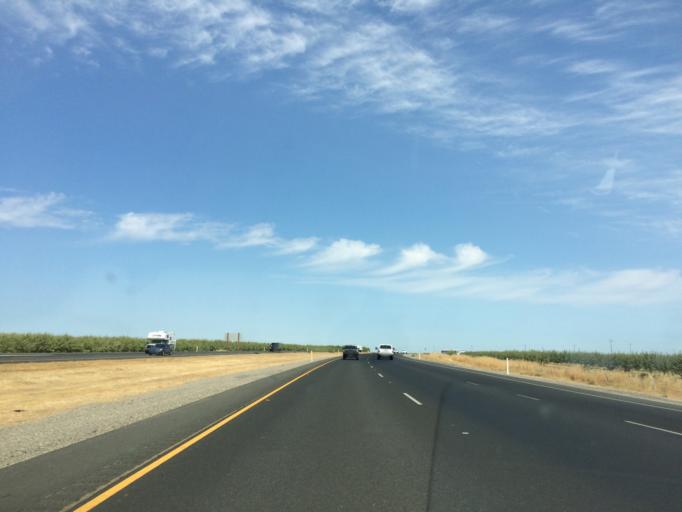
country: US
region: California
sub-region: Yolo County
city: Dunnigan
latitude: 38.9281
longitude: -122.0015
